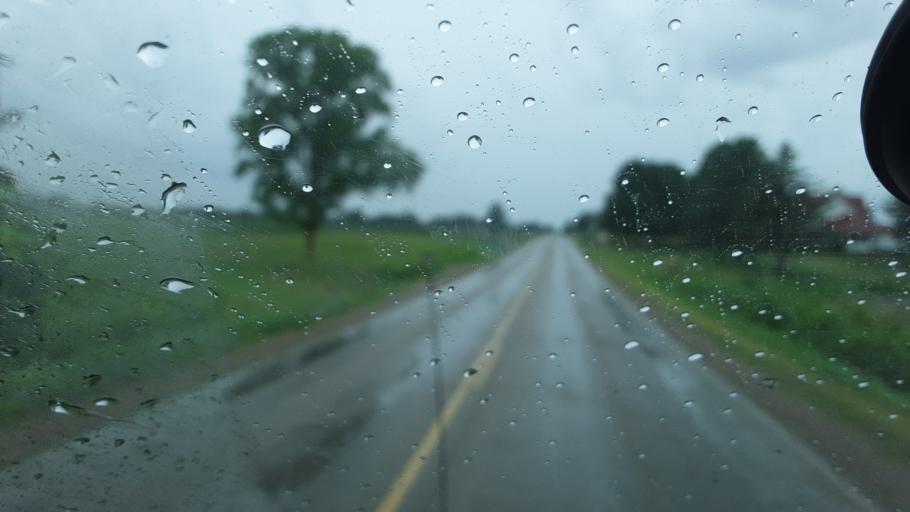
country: US
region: Ohio
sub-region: Williams County
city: Pioneer
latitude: 41.7089
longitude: -84.6225
